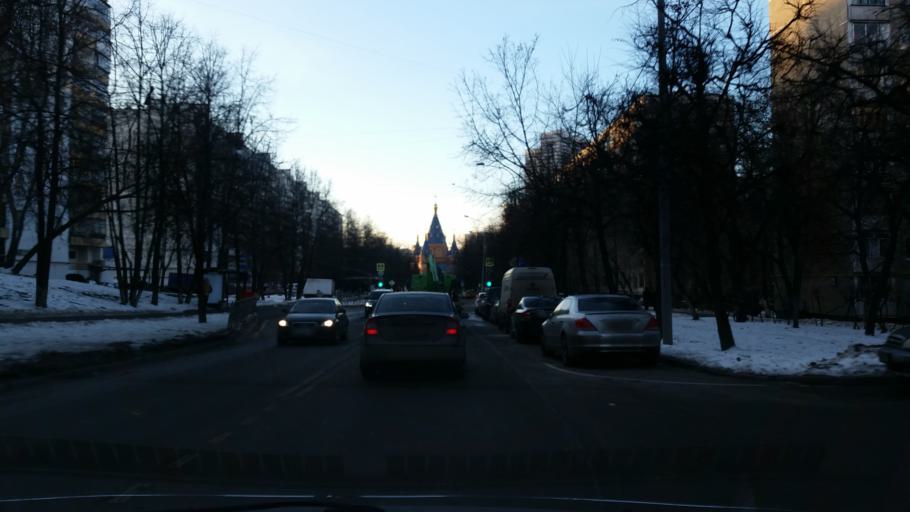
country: RU
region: Moscow
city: Nagornyy
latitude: 55.6340
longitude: 37.6095
